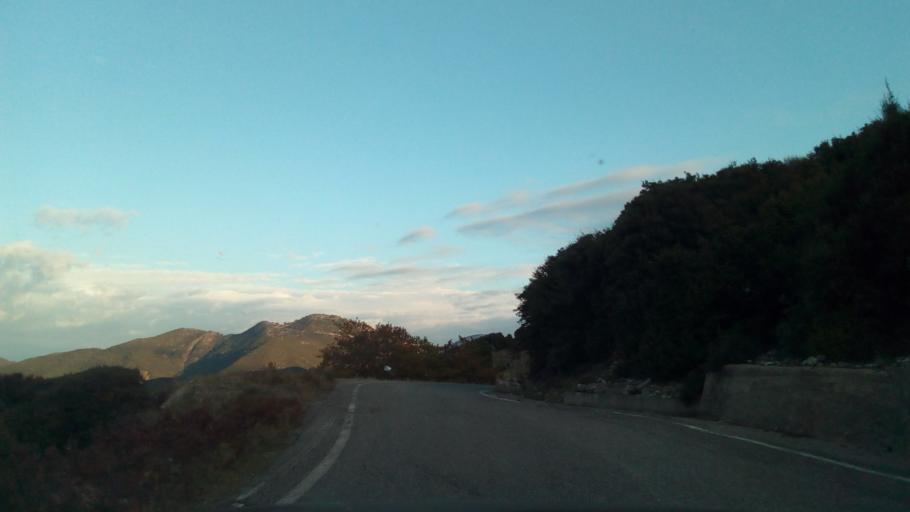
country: GR
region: West Greece
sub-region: Nomos Aitolias kai Akarnanias
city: Nafpaktos
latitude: 38.5063
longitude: 21.8355
